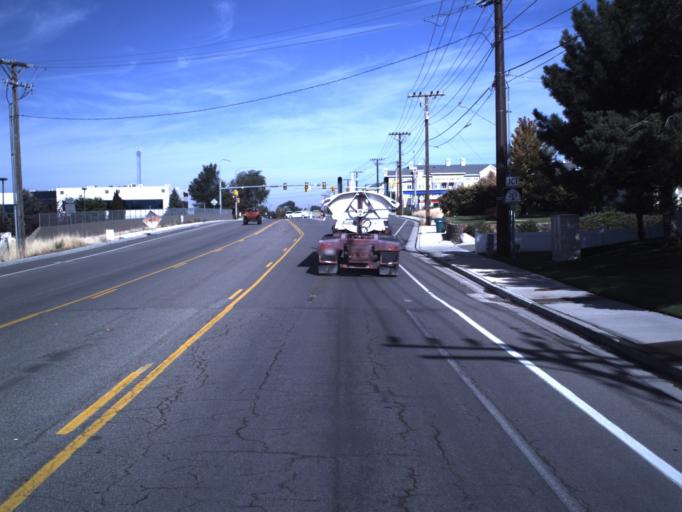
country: US
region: Utah
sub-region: Utah County
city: Orem
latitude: 40.2736
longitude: -111.7259
